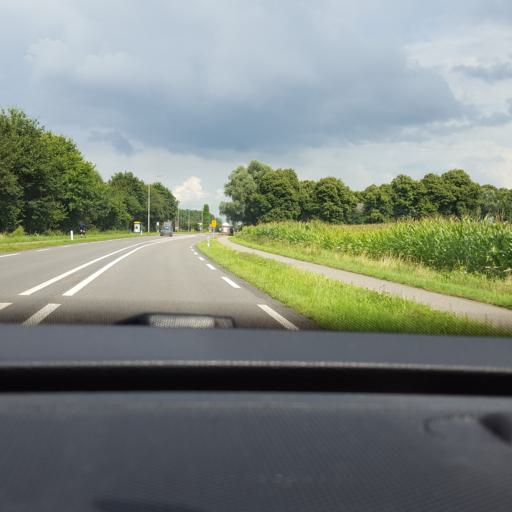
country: NL
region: Gelderland
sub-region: Gemeente Rheden
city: Rheden
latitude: 51.9850
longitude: 6.0176
